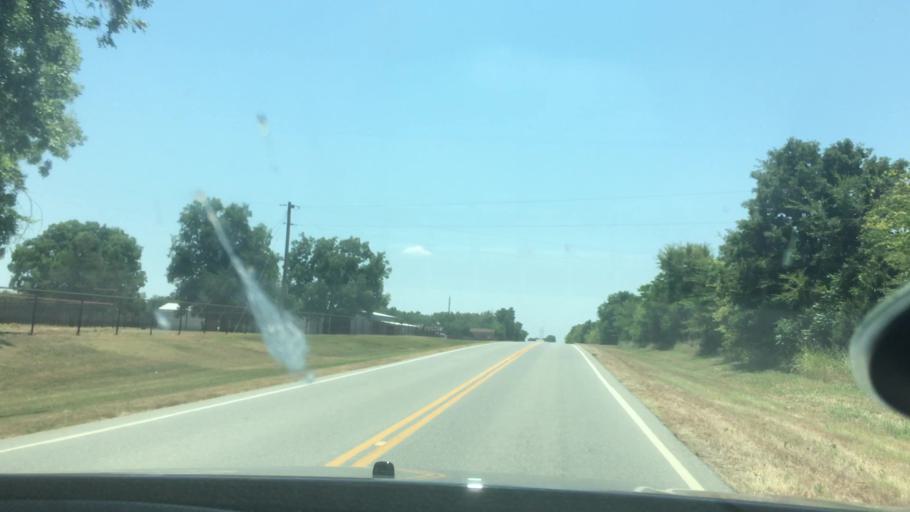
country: US
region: Oklahoma
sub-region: Coal County
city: Coalgate
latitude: 34.5321
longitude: -96.4070
